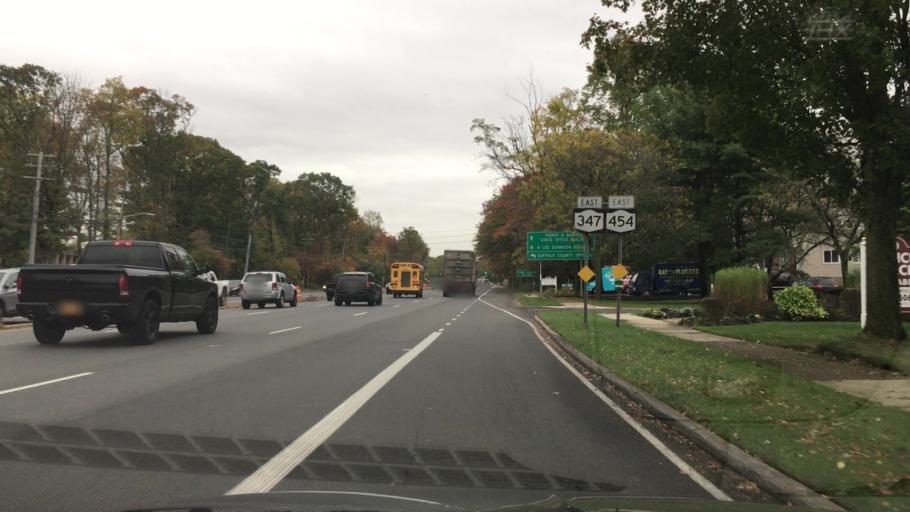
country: US
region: New York
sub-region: Suffolk County
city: Hauppauge
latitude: 40.8250
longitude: -73.2342
